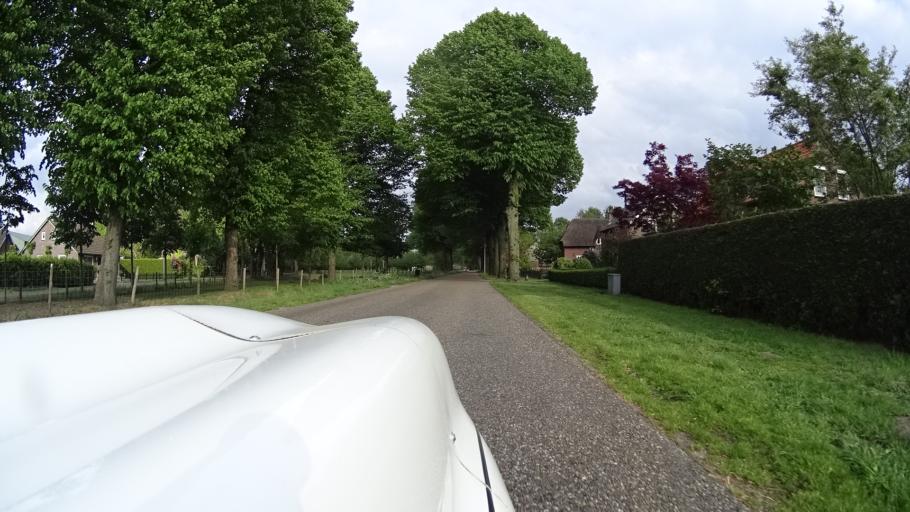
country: NL
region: North Brabant
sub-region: Gemeente Uden
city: Volkel
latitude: 51.6352
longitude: 5.6674
